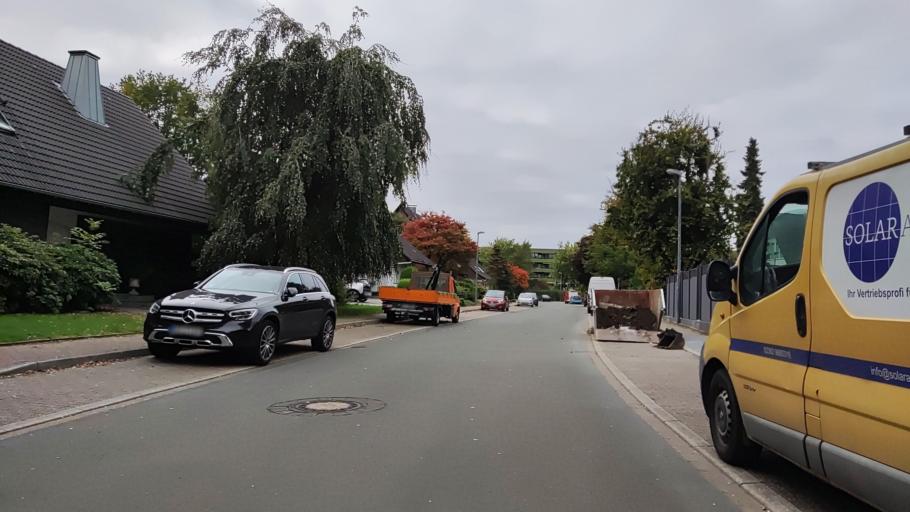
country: DE
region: North Rhine-Westphalia
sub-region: Regierungsbezirk Arnsberg
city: Herne
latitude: 51.5444
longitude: 7.2111
